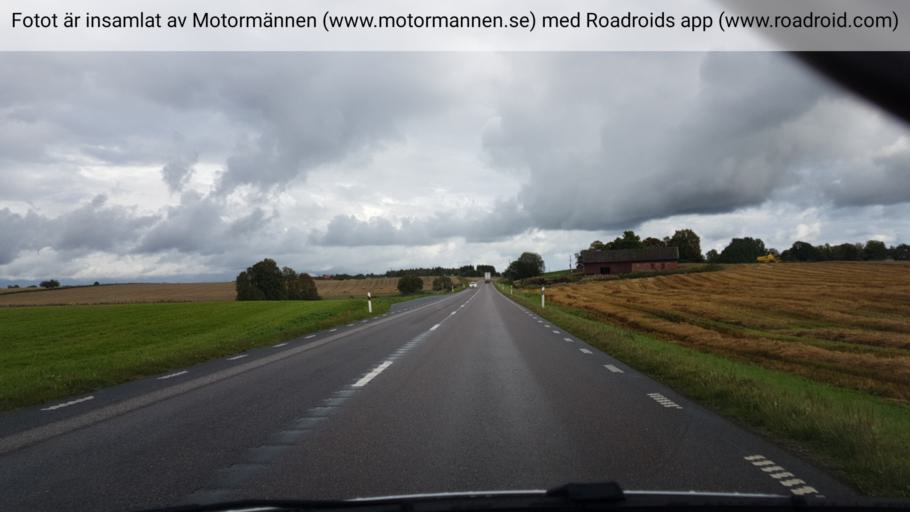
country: SE
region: Vaestra Goetaland
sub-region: Falkopings Kommun
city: Akarp
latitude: 58.1050
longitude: 13.7078
